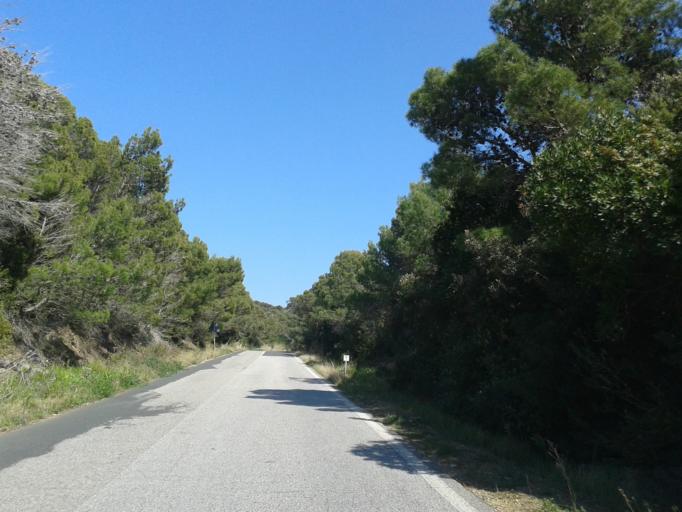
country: IT
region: Tuscany
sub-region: Provincia di Livorno
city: Quercianella
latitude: 43.4484
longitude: 10.3899
